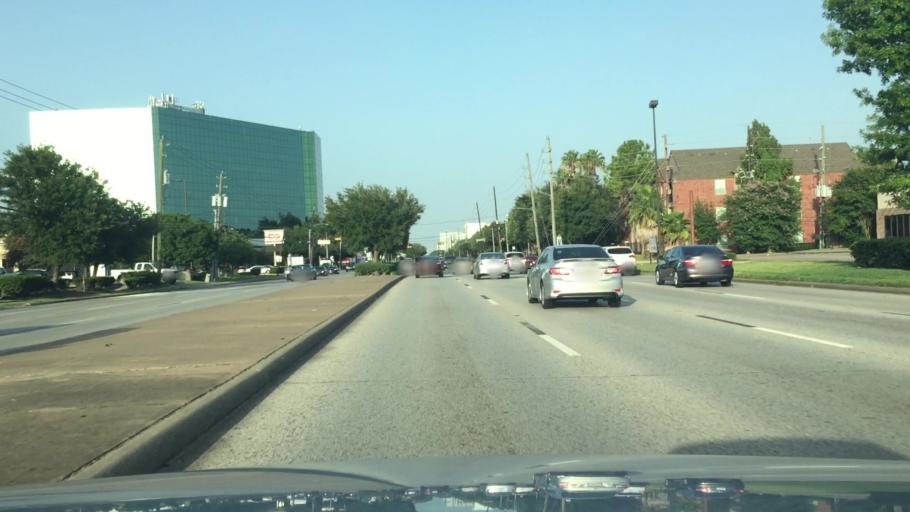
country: US
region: Texas
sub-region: Harris County
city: Bunker Hill Village
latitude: 29.7365
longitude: -95.5832
